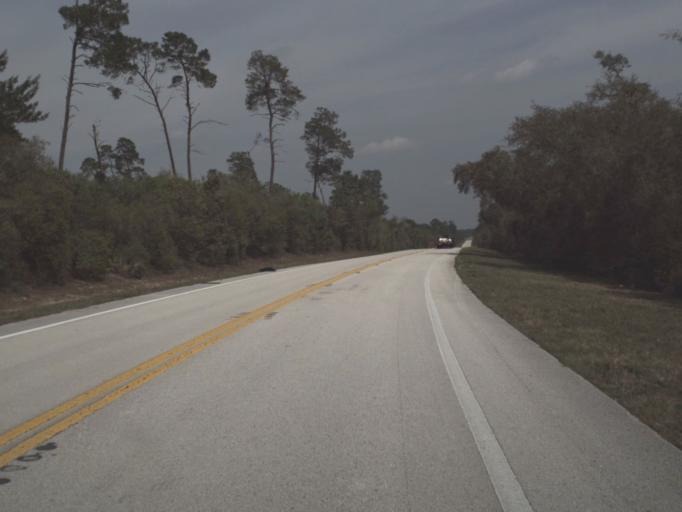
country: US
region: Florida
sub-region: Lake County
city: Astor
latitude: 29.1868
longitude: -81.6545
